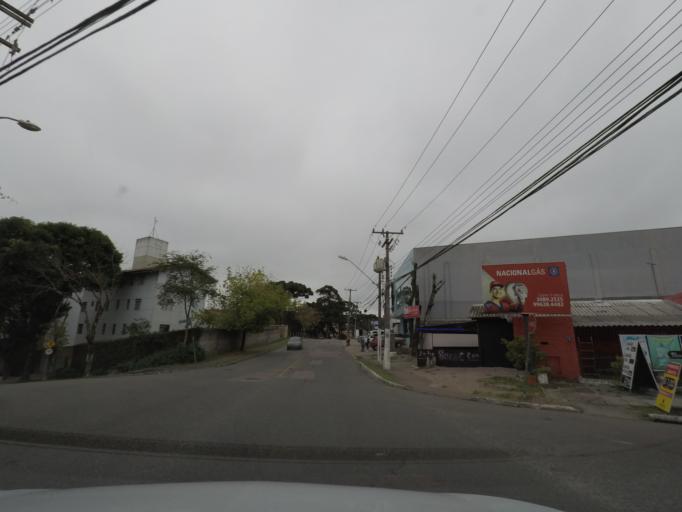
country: BR
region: Parana
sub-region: Curitiba
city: Curitiba
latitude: -25.4551
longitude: -49.3485
